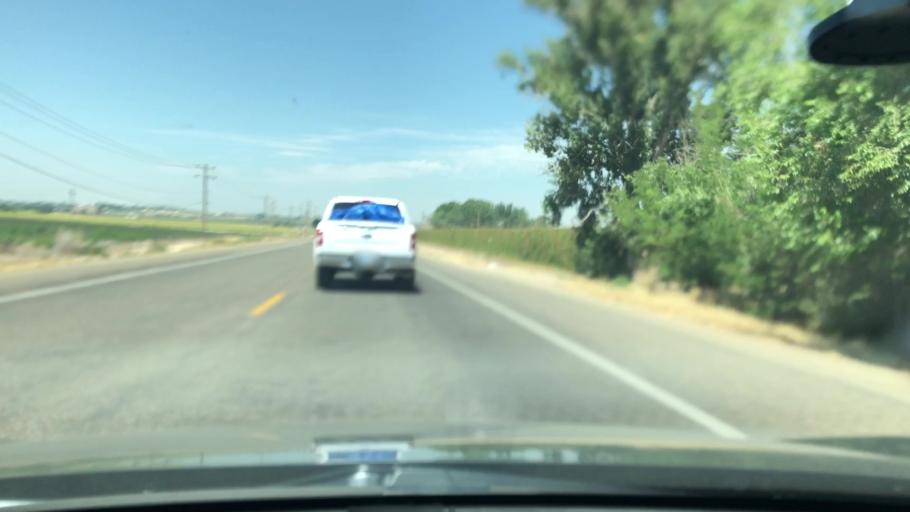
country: US
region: Idaho
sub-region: Owyhee County
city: Homedale
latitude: 43.6290
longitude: -116.9117
